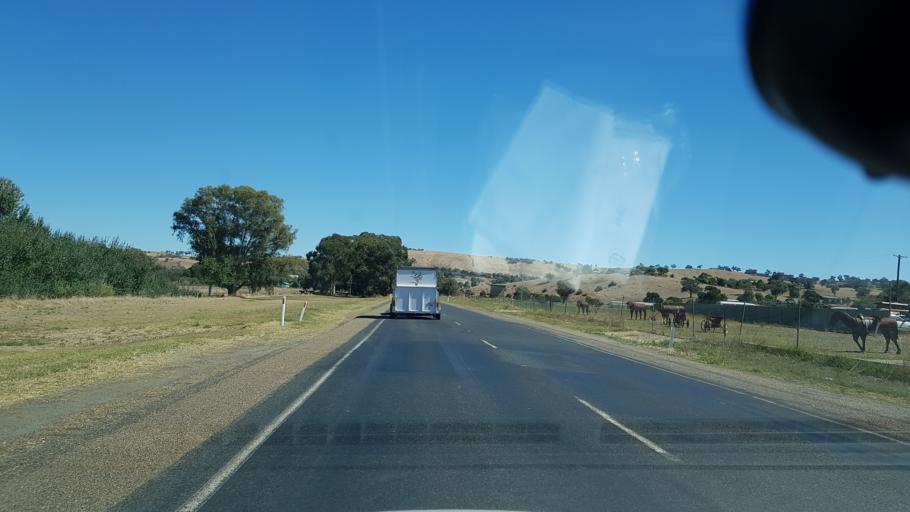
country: AU
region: New South Wales
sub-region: Gundagai
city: Gundagai
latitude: -34.8226
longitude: 148.3393
